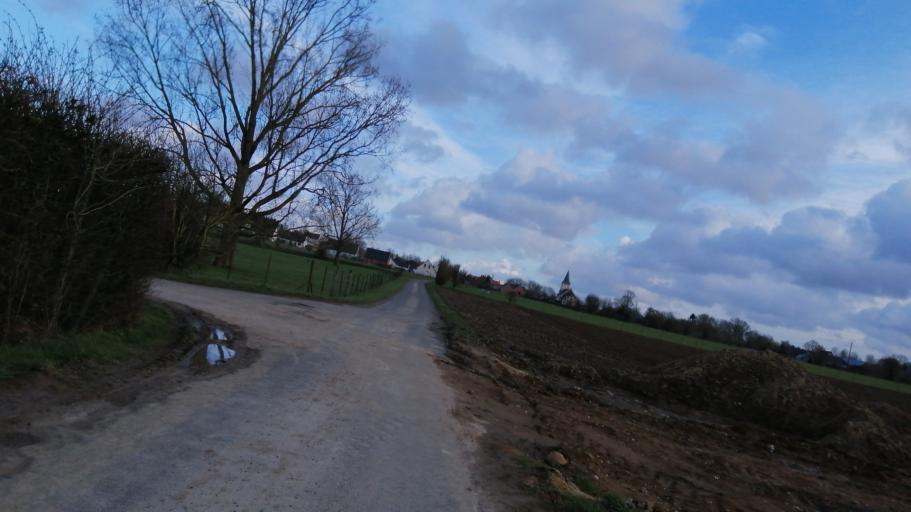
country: FR
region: Nord-Pas-de-Calais
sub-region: Departement du Pas-de-Calais
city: Beaurains
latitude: 50.2391
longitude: 2.7893
